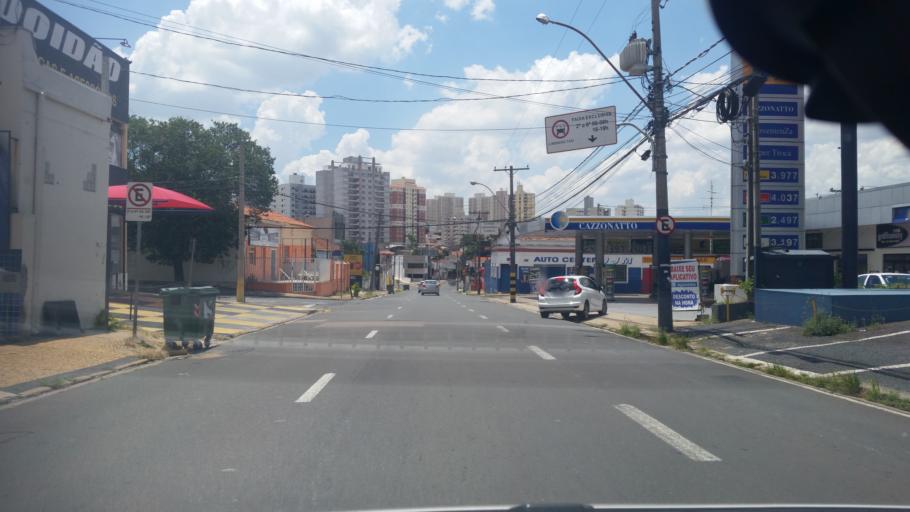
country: BR
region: Sao Paulo
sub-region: Campinas
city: Campinas
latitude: -22.8848
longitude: -47.0628
